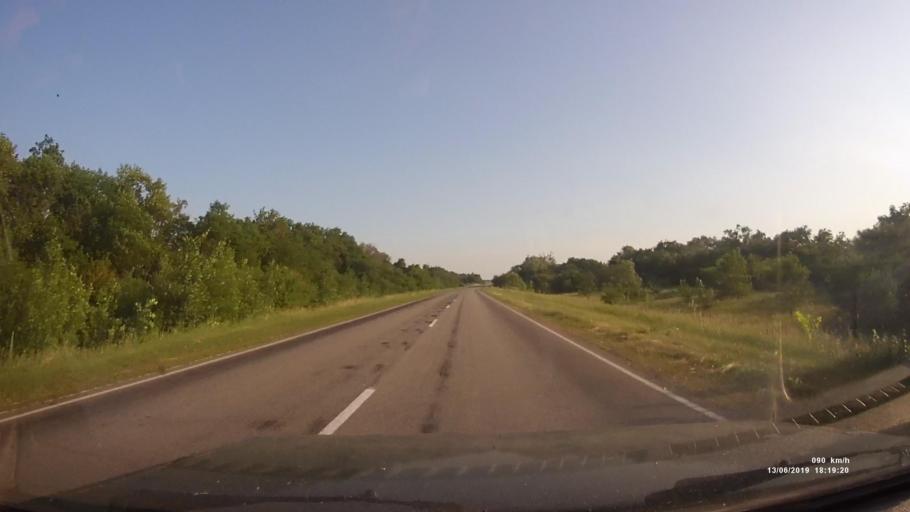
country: RU
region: Rostov
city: Kazanskaya
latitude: 49.8973
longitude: 41.3072
